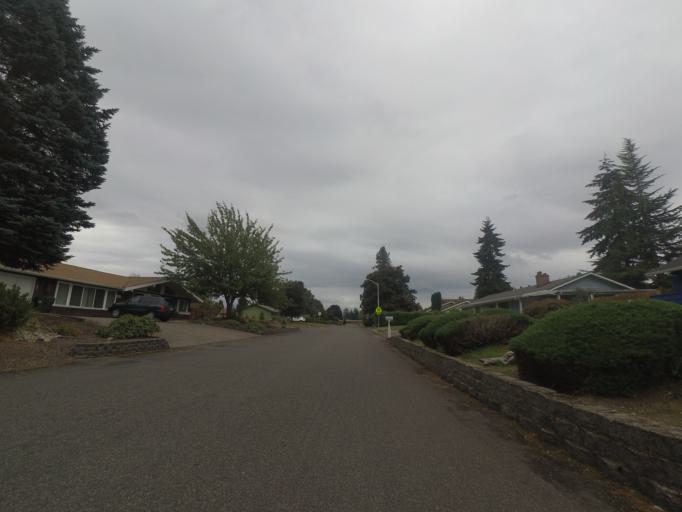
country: US
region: Washington
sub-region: Pierce County
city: Lakewood
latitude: 47.1518
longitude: -122.5091
